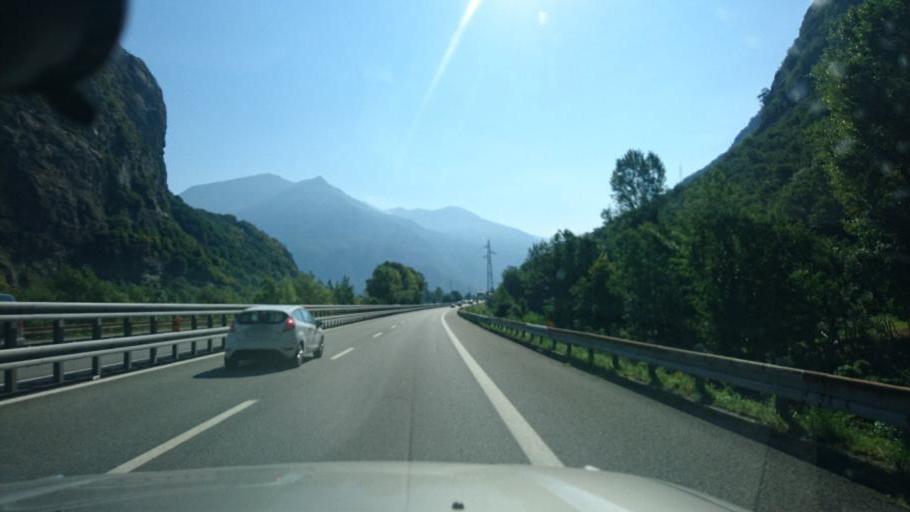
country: IT
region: Aosta Valley
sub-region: Valle d'Aosta
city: Bard
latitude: 45.6032
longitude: 7.7477
